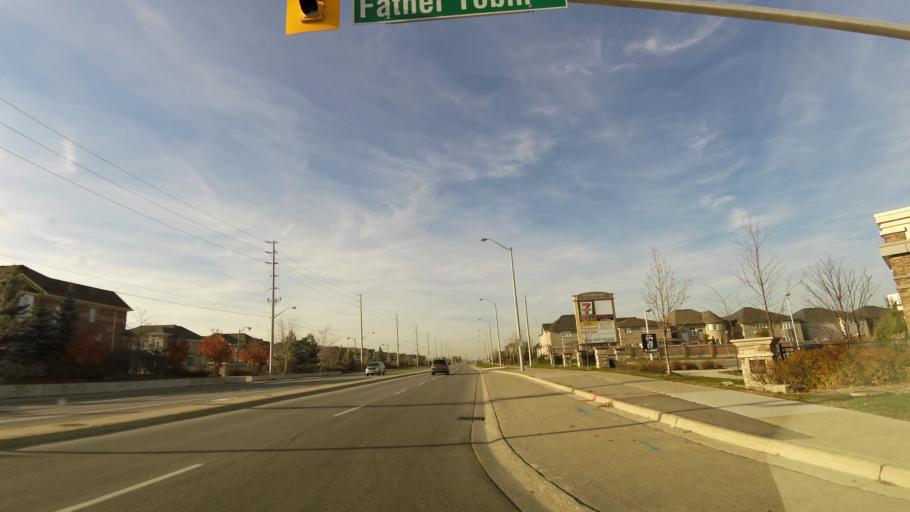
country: CA
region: Ontario
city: Brampton
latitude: 43.7711
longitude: -79.7565
